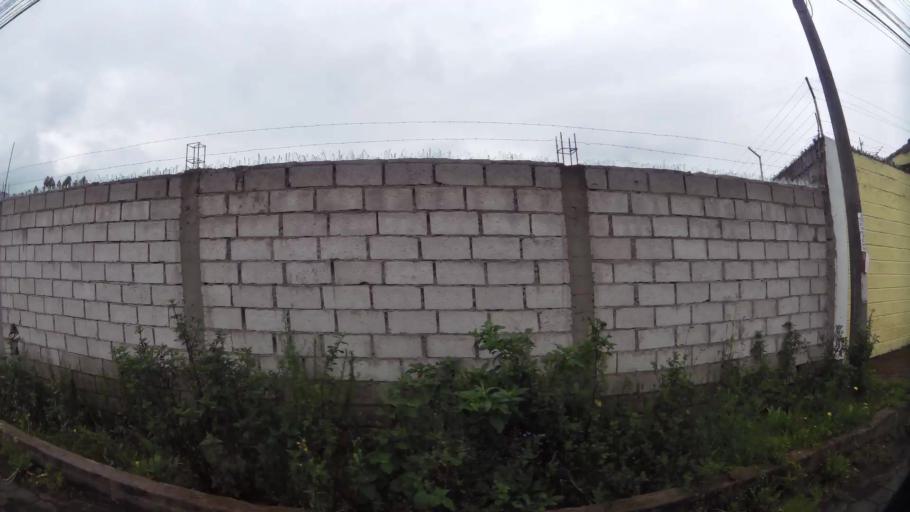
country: EC
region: Pichincha
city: Sangolqui
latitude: -0.2937
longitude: -78.4548
